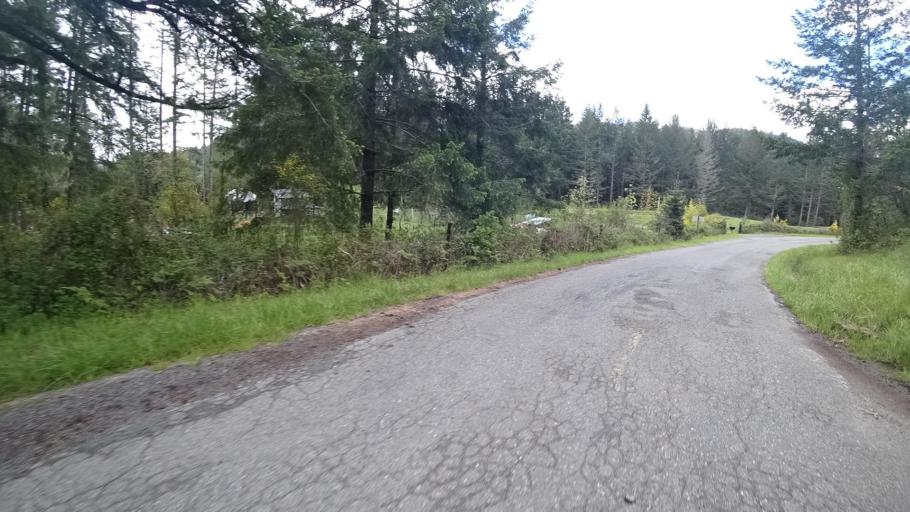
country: US
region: California
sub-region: Humboldt County
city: Blue Lake
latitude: 40.7580
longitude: -123.8777
